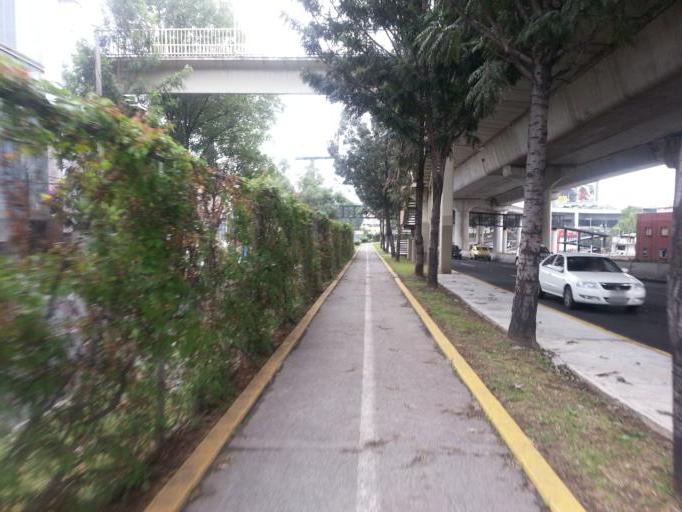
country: MX
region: Mexico City
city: Polanco
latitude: 19.4069
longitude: -99.1928
